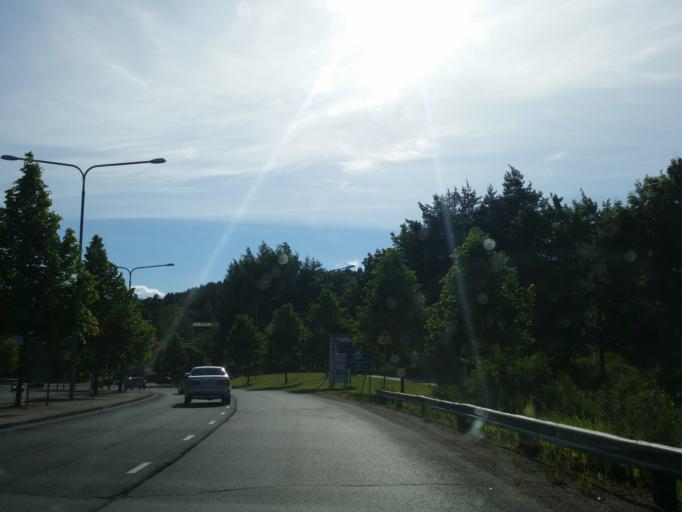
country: FI
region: Northern Savo
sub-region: Kuopio
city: Kuopio
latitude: 62.9058
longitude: 27.6834
